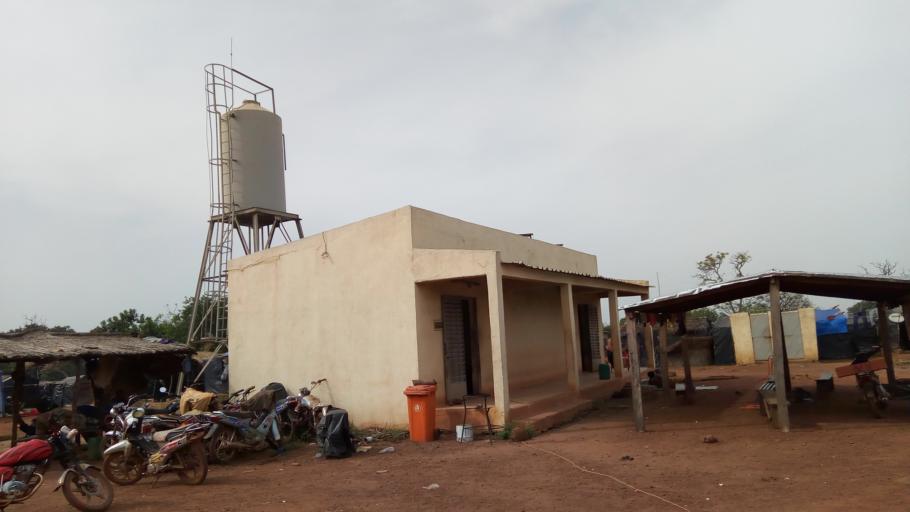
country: ML
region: Koulikoro
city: Kangaba
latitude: 11.6019
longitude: -8.6024
